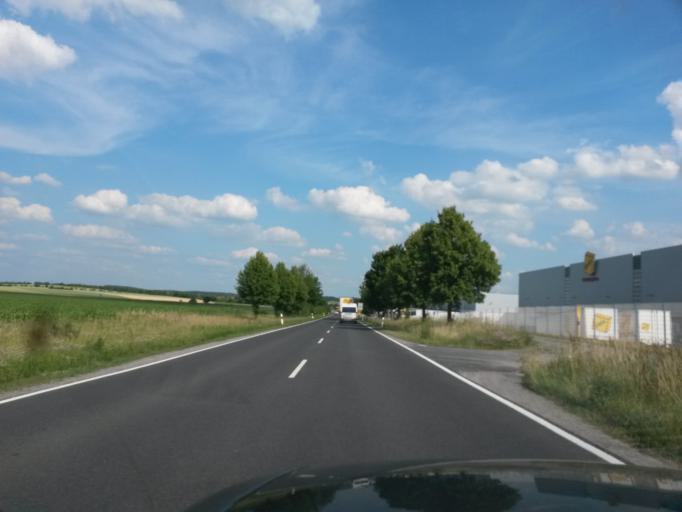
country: DE
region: Bavaria
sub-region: Regierungsbezirk Unterfranken
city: Kurnach
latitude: 49.8538
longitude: 10.0250
